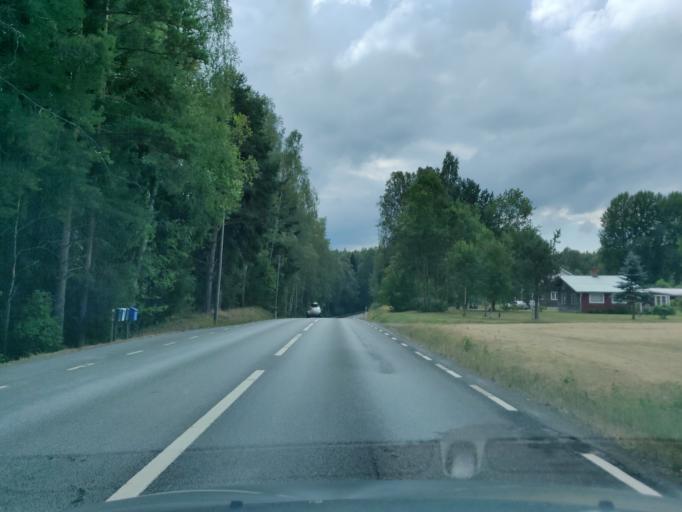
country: SE
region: Vaermland
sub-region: Munkfors Kommun
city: Munkfors
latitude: 59.8869
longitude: 13.5654
